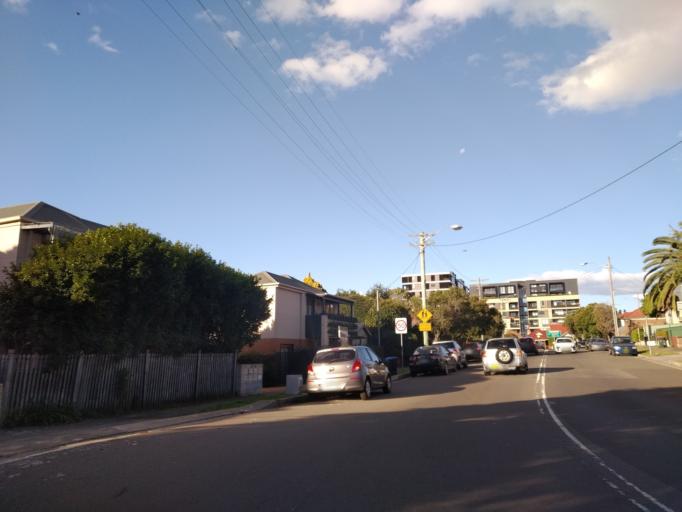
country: AU
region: New South Wales
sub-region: Ashfield
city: Summer Hill
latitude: -33.8888
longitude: 151.1457
